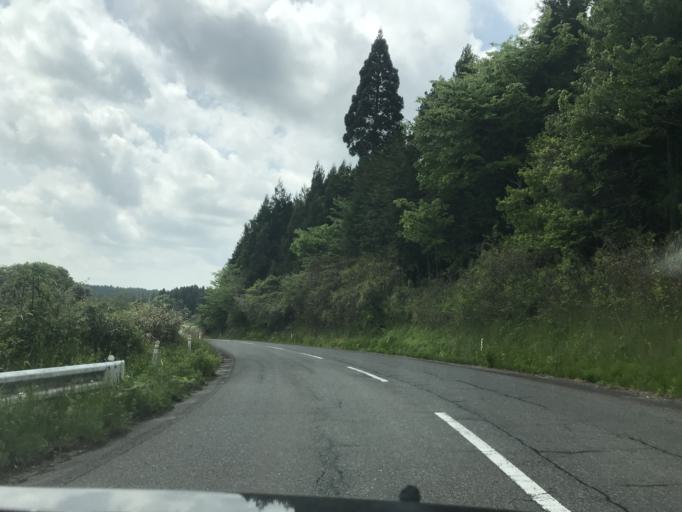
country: JP
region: Miyagi
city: Furukawa
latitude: 38.7102
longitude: 140.9180
